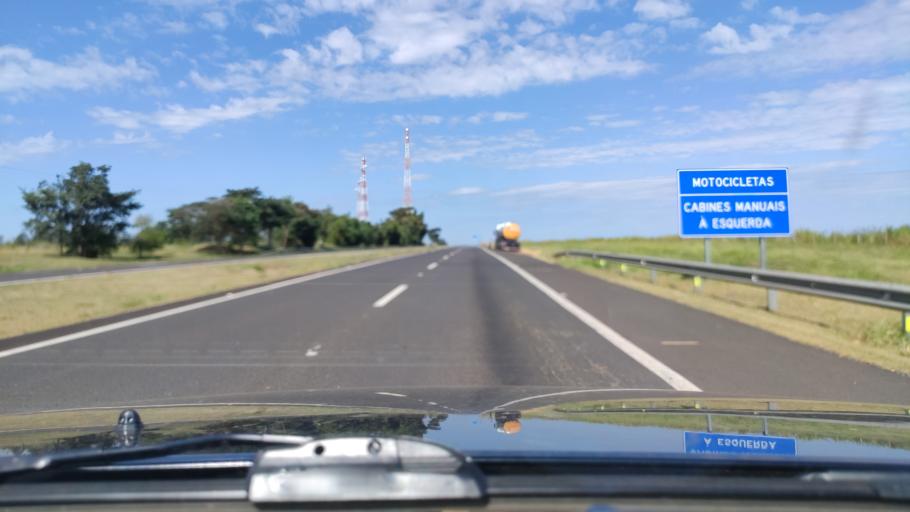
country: BR
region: Sao Paulo
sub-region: Rancharia
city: Rancharia
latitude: -22.4267
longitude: -51.0227
